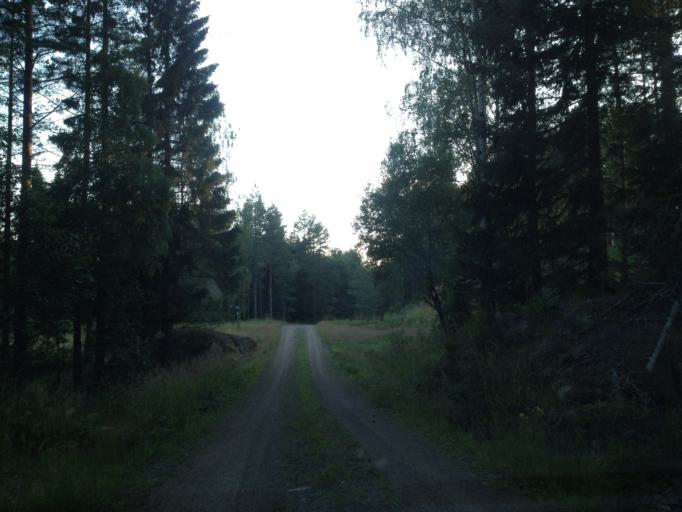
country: SE
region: Kalmar
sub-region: Vasterviks Kommun
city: Overum
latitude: 57.9978
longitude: 16.1411
